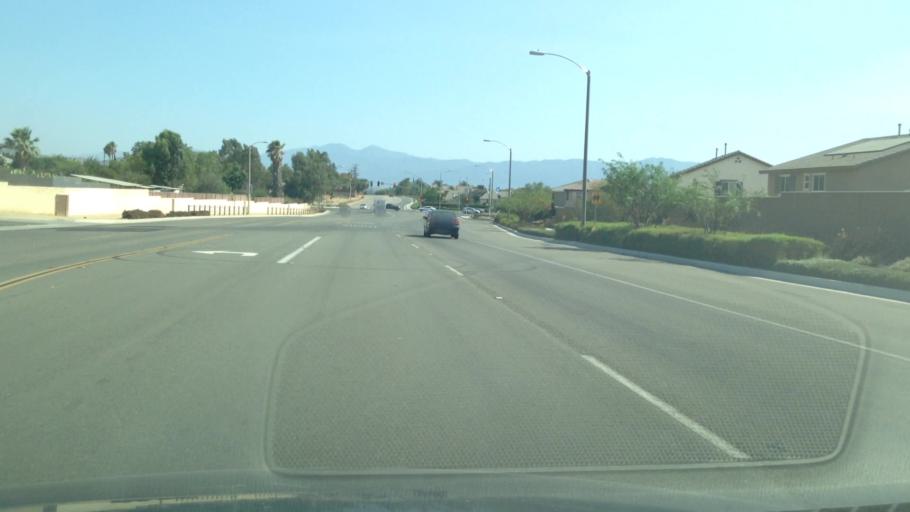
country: US
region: California
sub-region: Riverside County
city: Mira Loma
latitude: 33.9775
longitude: -117.5406
